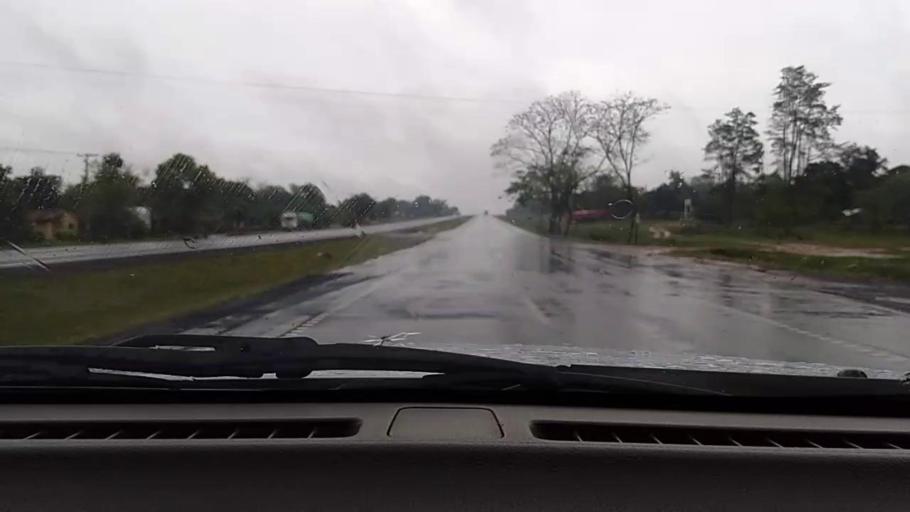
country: PY
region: Caaguazu
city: Repatriacion
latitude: -25.4664
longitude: -55.9366
